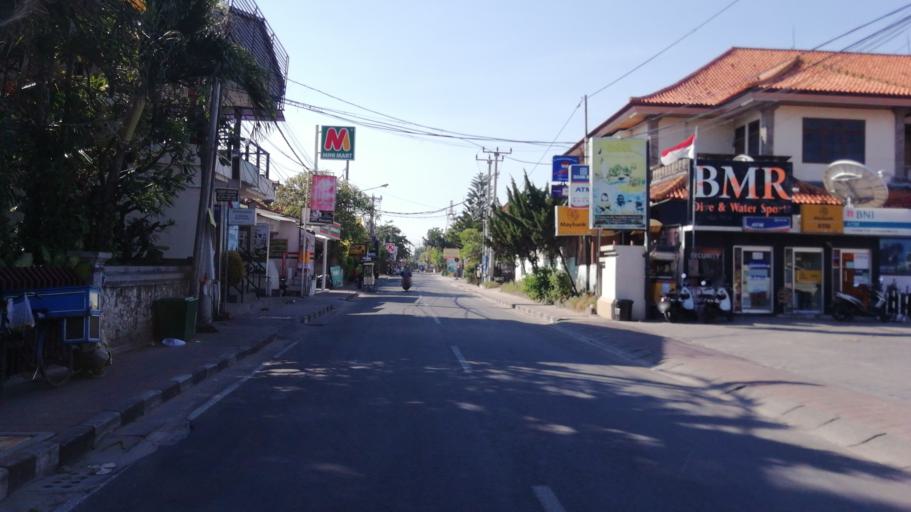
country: ID
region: Bali
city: Bualu
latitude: -8.7582
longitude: 115.2215
